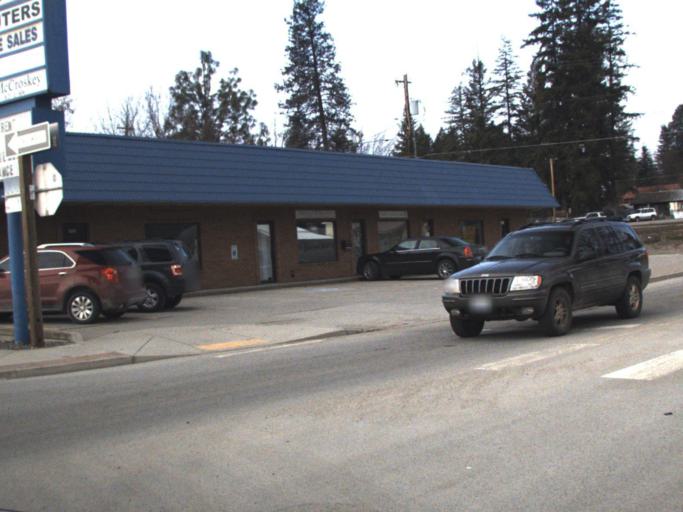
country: US
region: Washington
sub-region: Pend Oreille County
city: Newport
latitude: 48.1840
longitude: -117.0441
